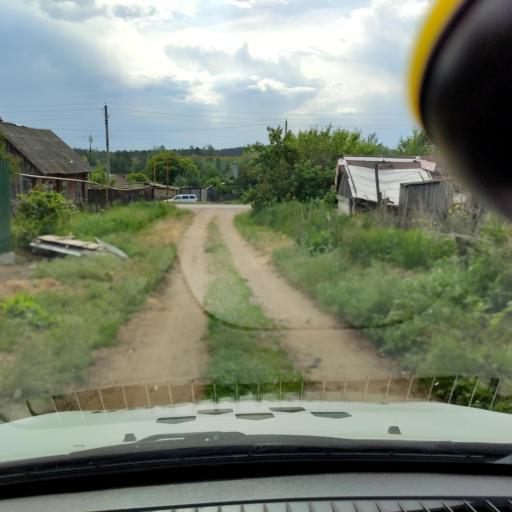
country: RU
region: Samara
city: Zhigulevsk
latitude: 53.5461
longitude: 49.5280
